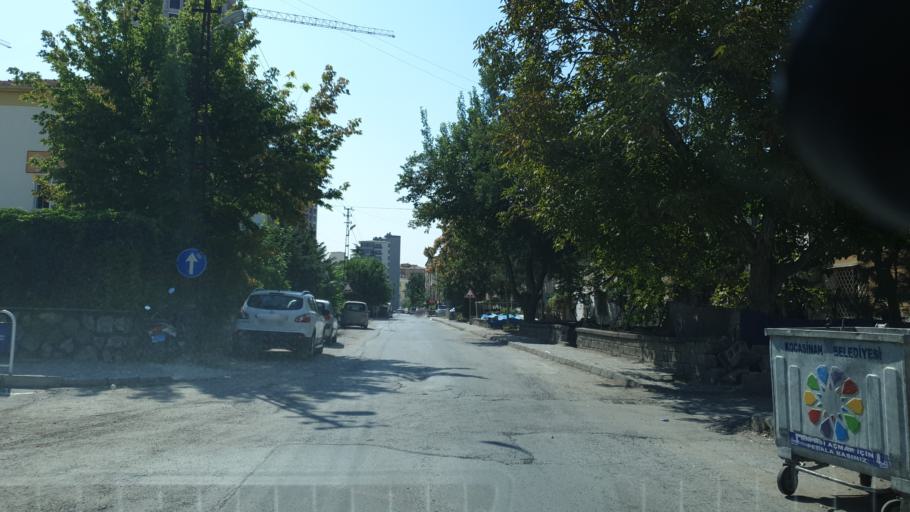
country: TR
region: Kayseri
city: Kayseri
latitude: 38.7294
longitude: 35.4889
